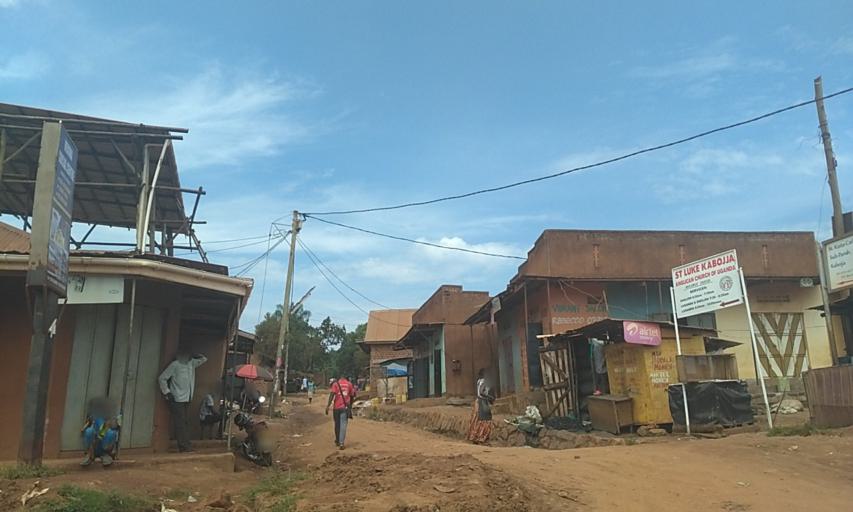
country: UG
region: Central Region
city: Kampala Central Division
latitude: 0.2863
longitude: 32.5177
